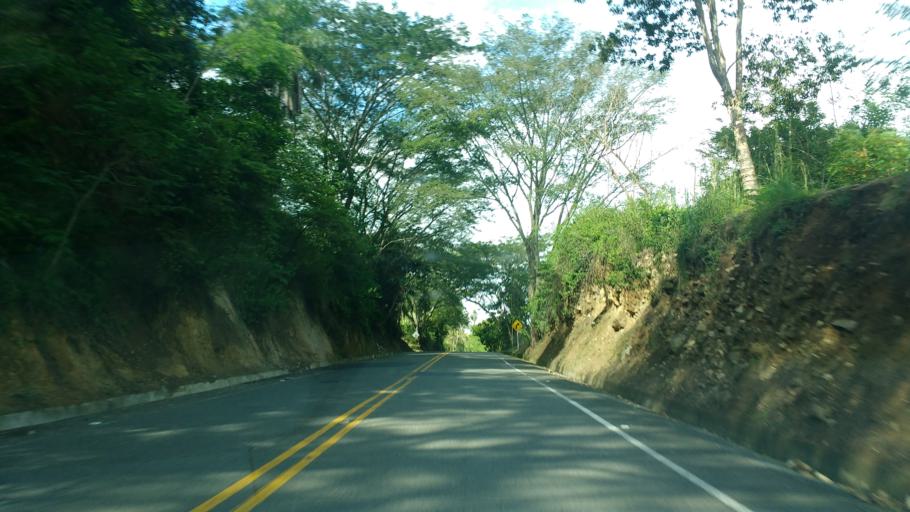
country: CO
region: Antioquia
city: Concordia
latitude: 6.0653
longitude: -75.8620
